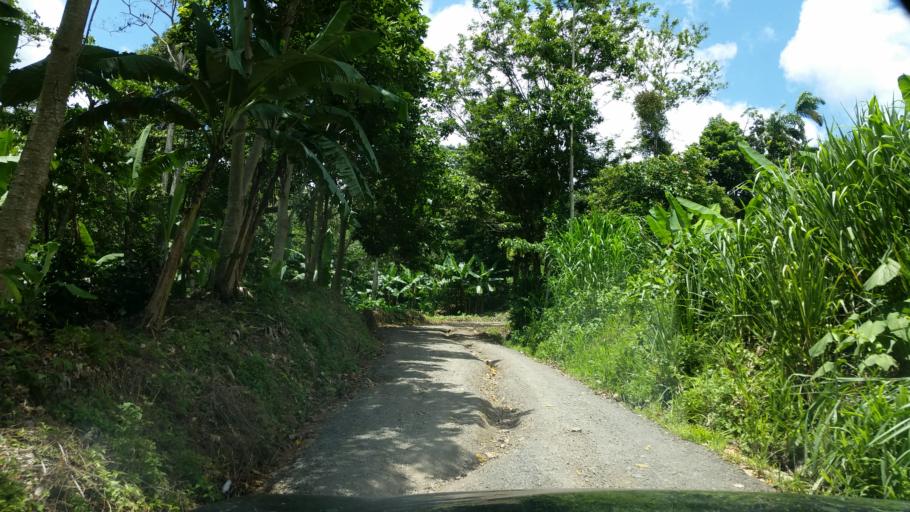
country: NI
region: Atlantico Norte (RAAN)
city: Waslala
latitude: 13.2522
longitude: -85.6150
